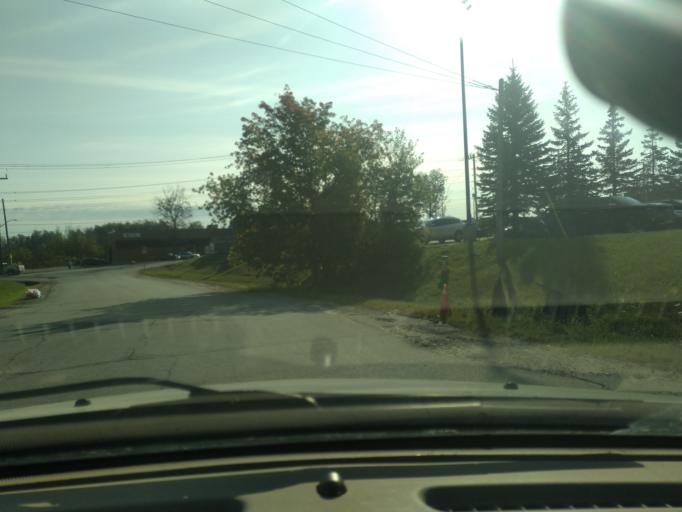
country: CA
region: Ontario
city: Barrie
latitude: 44.3549
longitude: -79.6667
